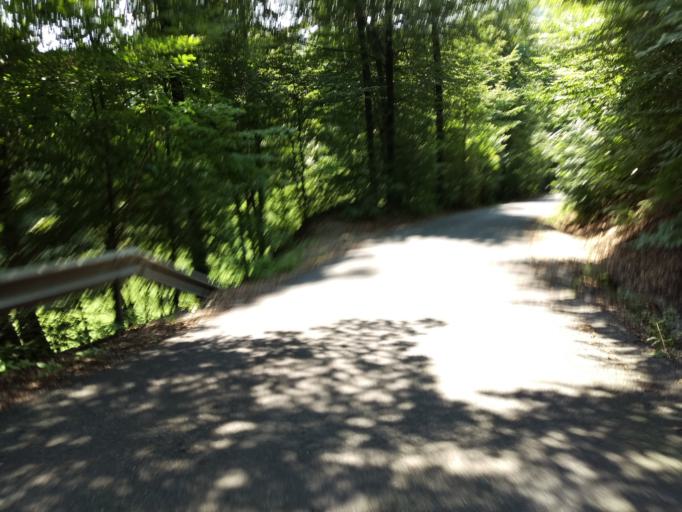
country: AT
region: Styria
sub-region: Politischer Bezirk Graz-Umgebung
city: Hart bei Graz
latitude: 47.0514
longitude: 15.5469
